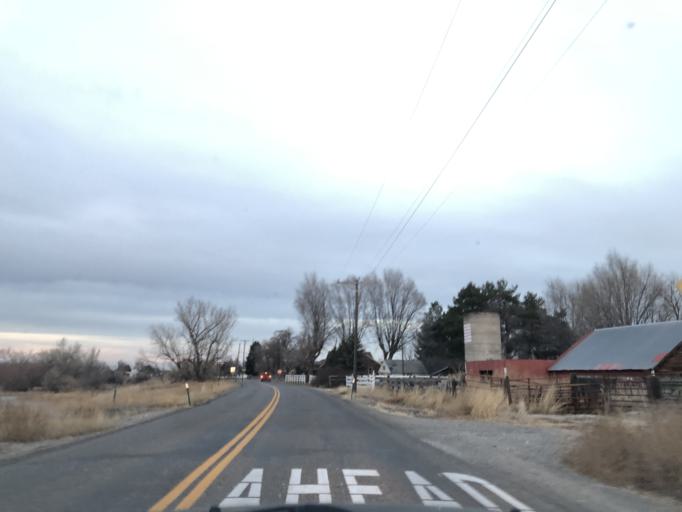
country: US
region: Utah
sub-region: Cache County
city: Benson
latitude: 41.7934
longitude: -111.9062
